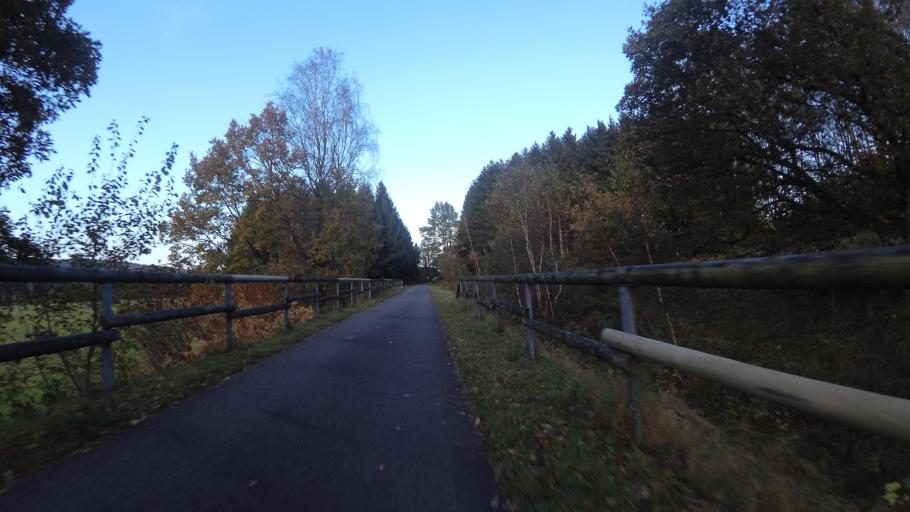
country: DE
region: Rheinland-Pfalz
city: Kell
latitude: 49.6412
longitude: 6.8358
